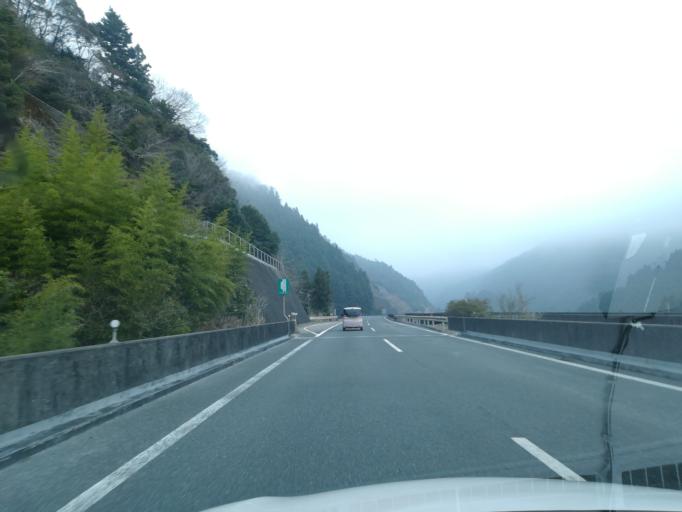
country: JP
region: Ehime
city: Kawanoecho
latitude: 33.7815
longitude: 133.6613
